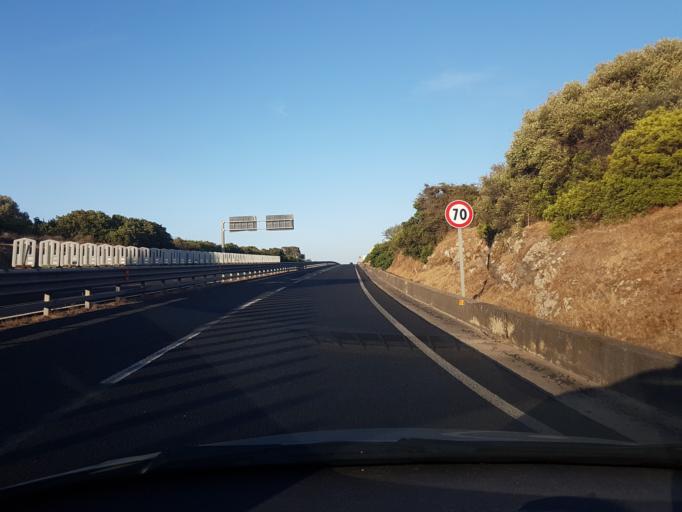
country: IT
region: Sardinia
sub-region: Provincia di Oristano
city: Paulilatino
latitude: 40.0909
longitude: 8.7590
